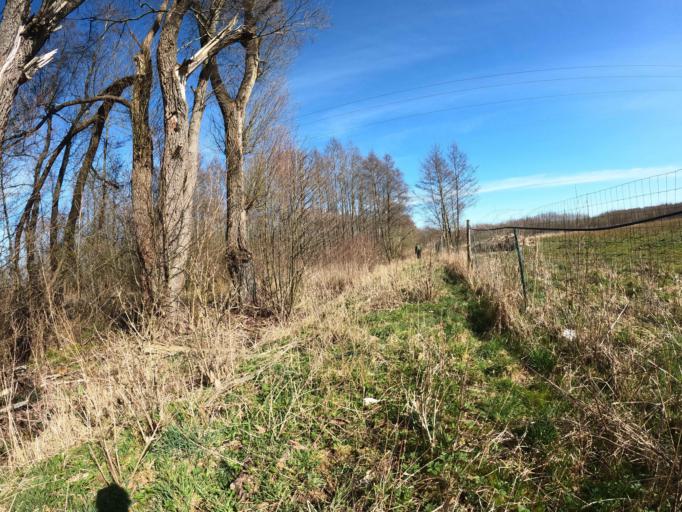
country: PL
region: West Pomeranian Voivodeship
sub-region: Powiat gryficki
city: Brojce
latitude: 53.9262
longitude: 15.2940
